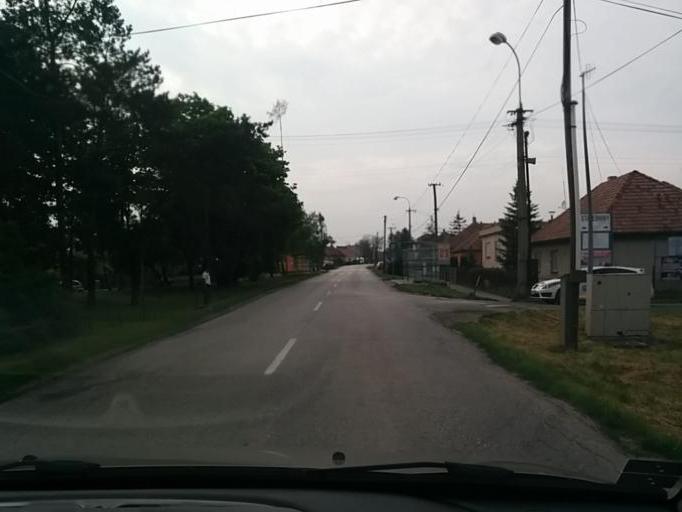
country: SK
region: Trnavsky
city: Sladkovicovo
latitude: 48.2260
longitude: 17.5790
